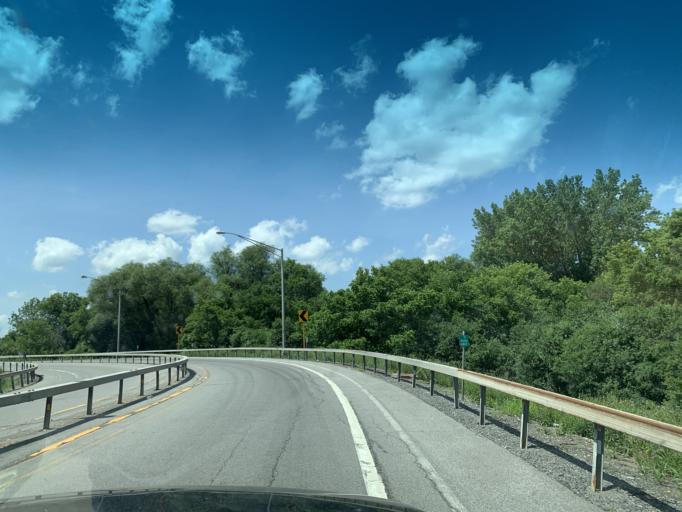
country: US
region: New York
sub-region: Oneida County
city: New Hartford
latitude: 43.0819
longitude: -75.2923
